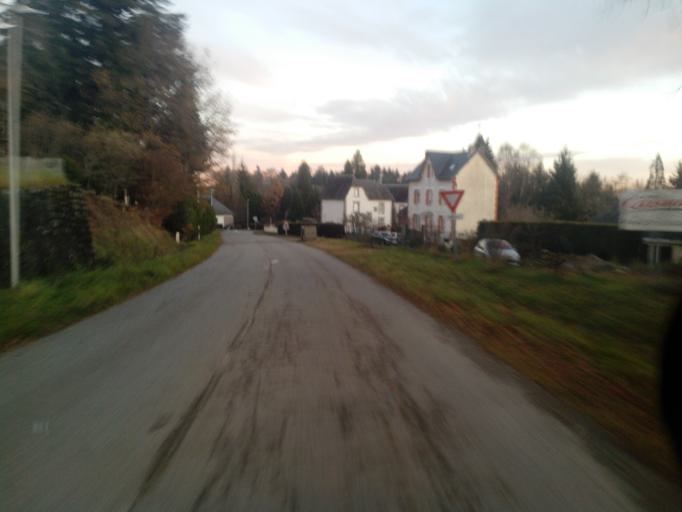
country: FR
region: Limousin
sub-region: Departement de la Correze
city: Meymac
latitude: 45.5451
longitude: 2.1375
